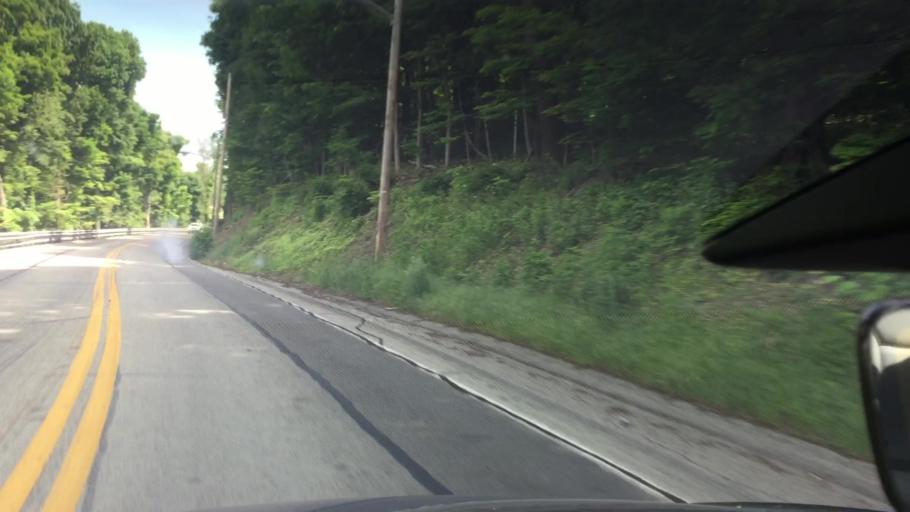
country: US
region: Pennsylvania
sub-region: Allegheny County
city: Penn Hills
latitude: 40.4787
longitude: -79.8391
